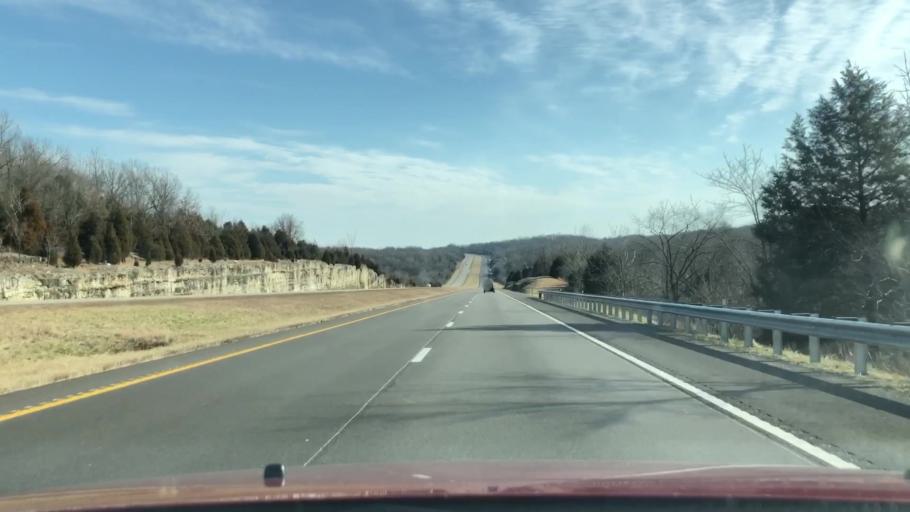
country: US
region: Missouri
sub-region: Wright County
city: Mansfield
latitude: 37.1125
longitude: -92.6634
